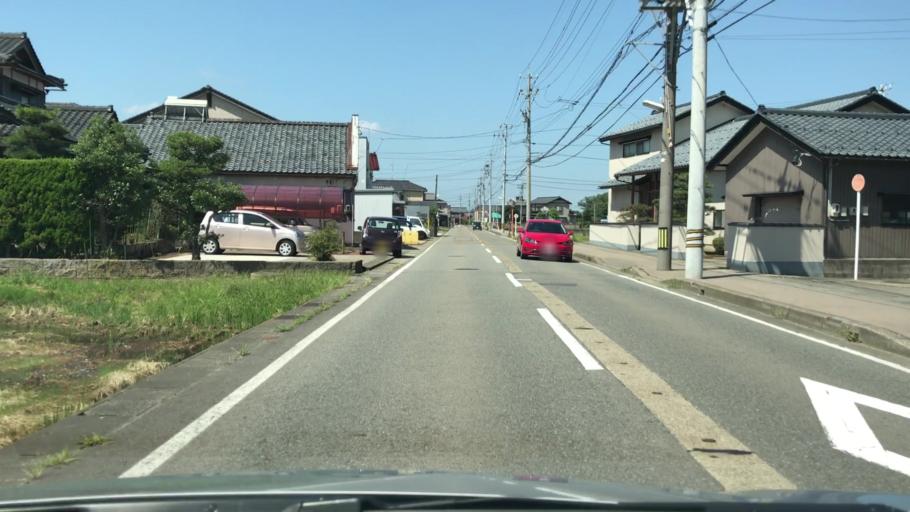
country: JP
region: Fukui
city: Maruoka
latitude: 36.1299
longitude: 136.2135
